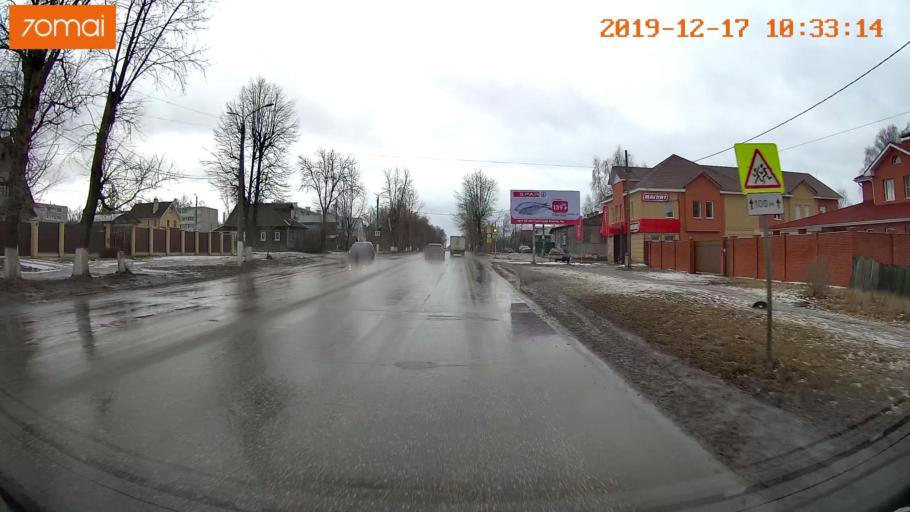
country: RU
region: Vladimir
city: Gus'-Khrustal'nyy
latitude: 55.6239
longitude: 40.6825
